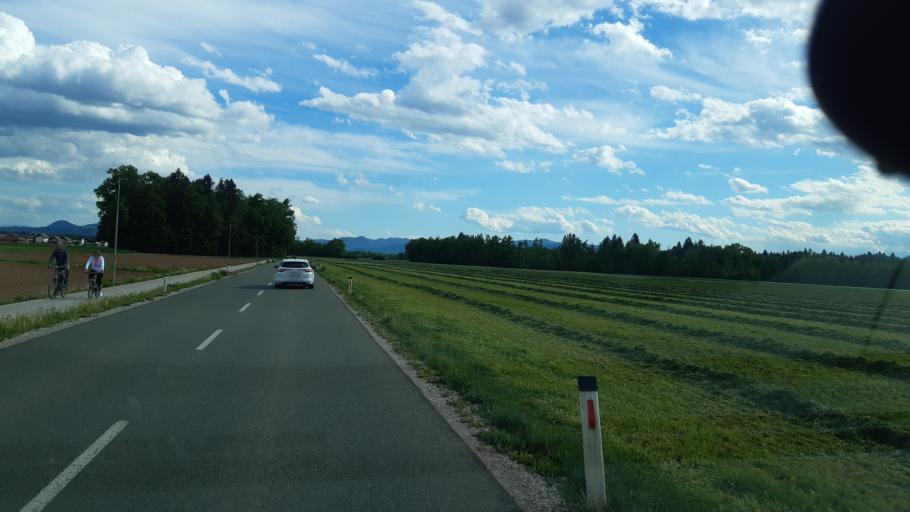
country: SI
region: Sencur
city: Sencur
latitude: 46.2609
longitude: 14.4184
